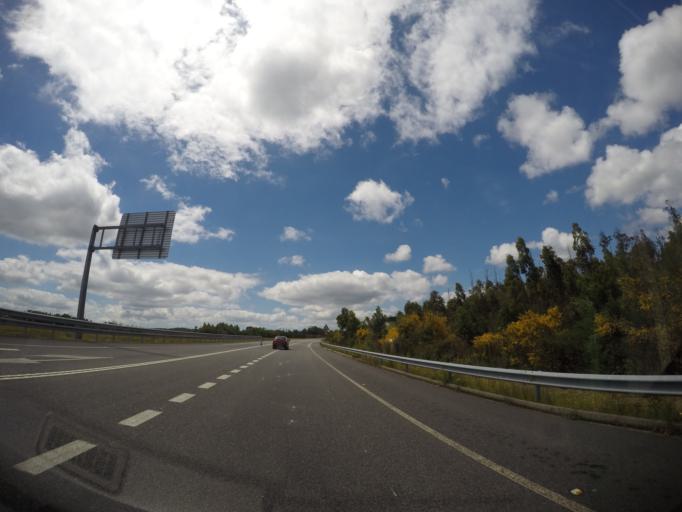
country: ES
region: Aragon
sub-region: Provincia de Zaragoza
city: Pina de Ebro
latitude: 41.5338
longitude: -0.4995
